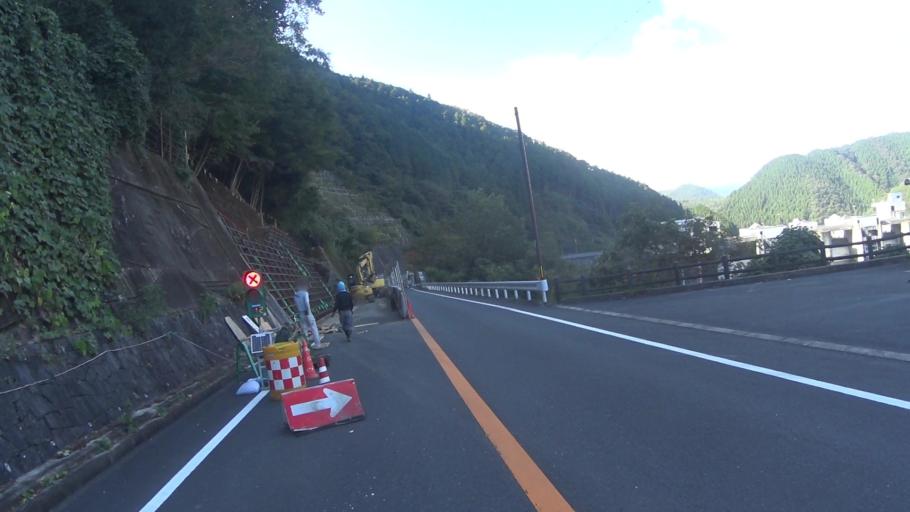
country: JP
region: Kyoto
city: Kameoka
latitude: 35.1457
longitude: 135.5172
